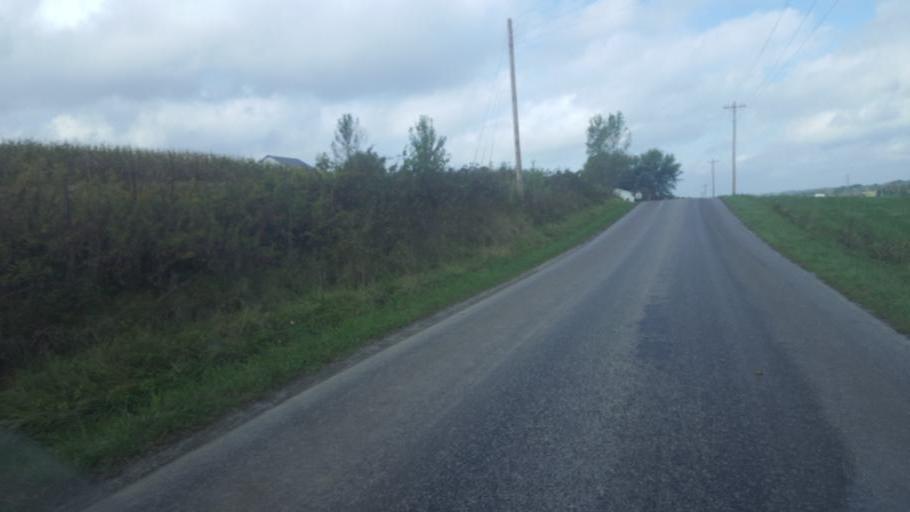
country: US
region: Ohio
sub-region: Wayne County
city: Apple Creek
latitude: 40.6499
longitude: -81.8612
